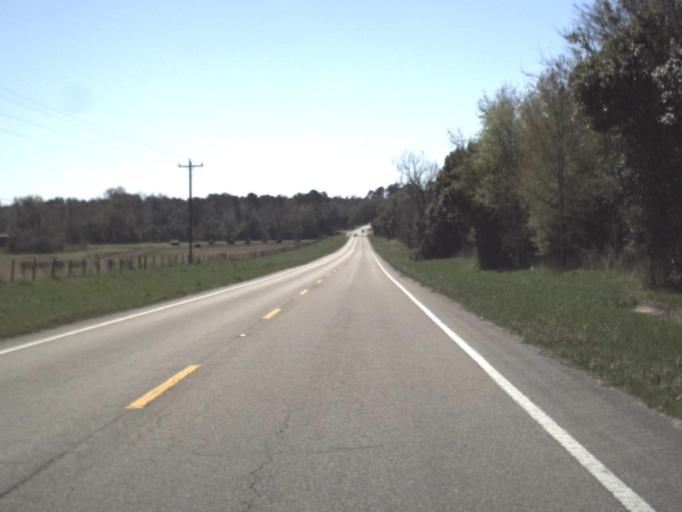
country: US
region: Florida
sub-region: Jefferson County
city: Monticello
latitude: 30.3642
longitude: -83.9901
